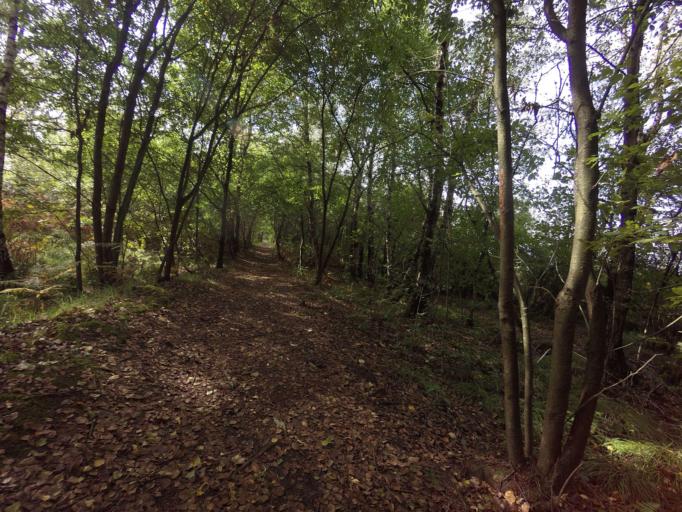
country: NL
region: Overijssel
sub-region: Gemeente Enschede
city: Enschede
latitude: 52.1855
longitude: 6.9567
